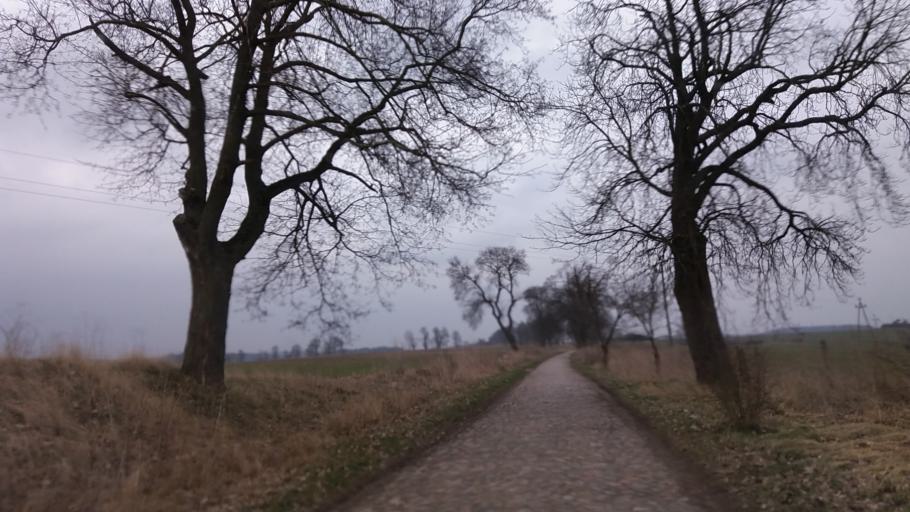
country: PL
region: West Pomeranian Voivodeship
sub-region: Powiat choszczenski
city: Krzecin
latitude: 53.1413
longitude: 15.5572
